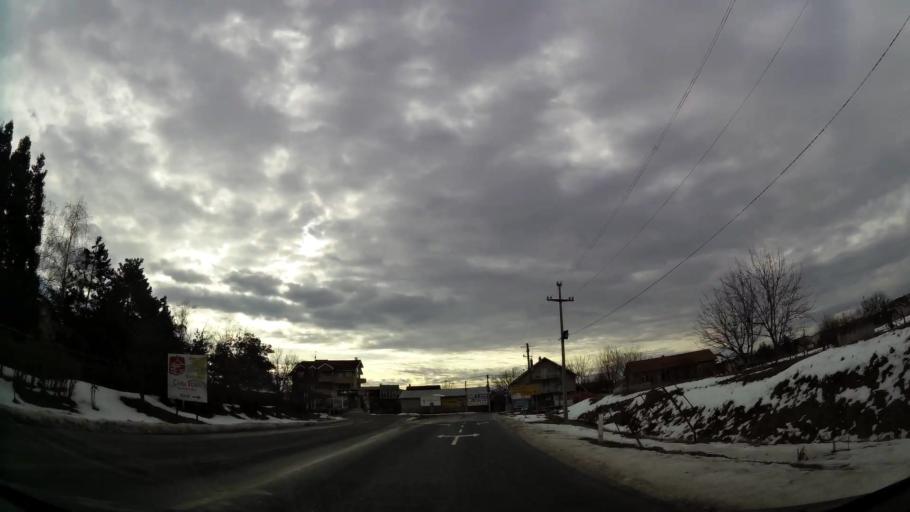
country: RS
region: Central Serbia
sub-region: Belgrade
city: Surcin
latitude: 44.7993
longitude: 20.3205
